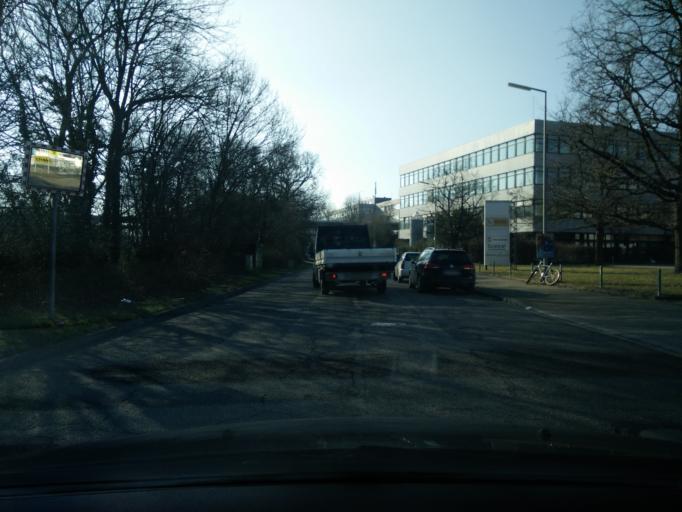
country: DE
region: Baden-Wuerttemberg
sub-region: Karlsruhe Region
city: Karlsruhe
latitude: 48.9968
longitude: 8.3726
